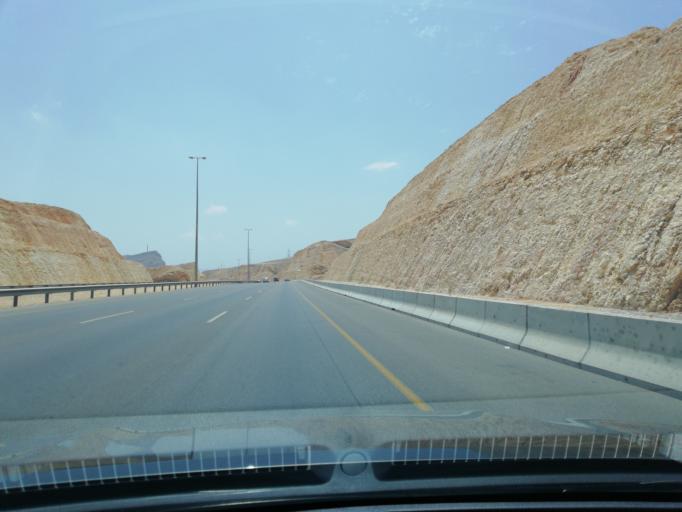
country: OM
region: Muhafazat Masqat
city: As Sib al Jadidah
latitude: 23.5481
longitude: 58.2370
